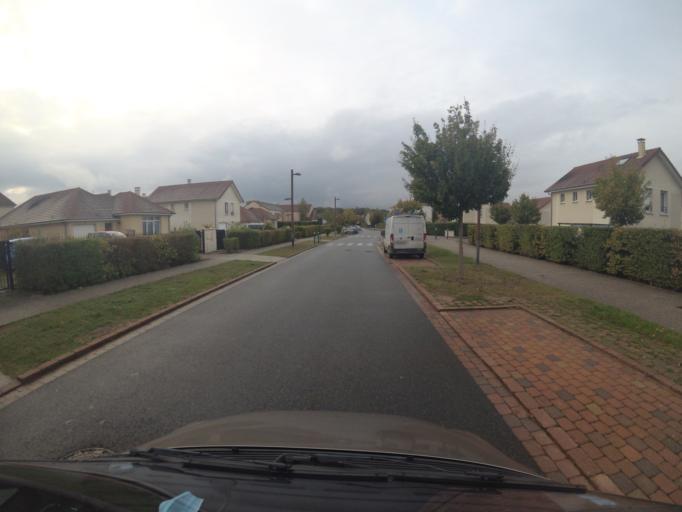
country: FR
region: Ile-de-France
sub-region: Departement de Seine-et-Marne
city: Chanteloup-en-Brie
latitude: 48.8602
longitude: 2.7406
